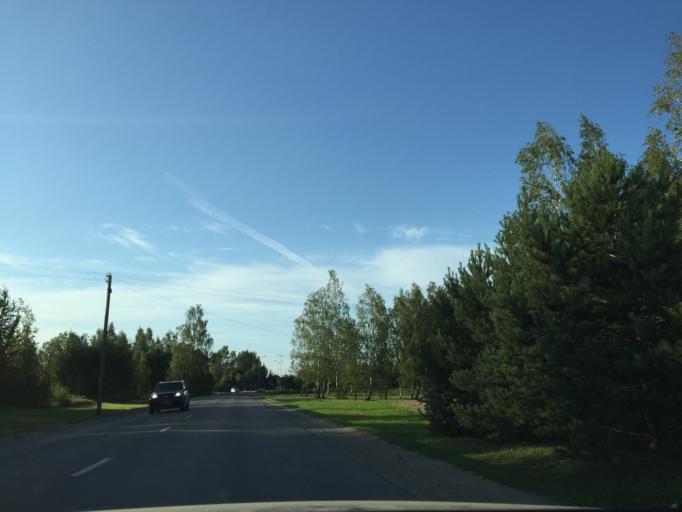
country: LT
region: Panevezys
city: Rokiskis
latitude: 55.9502
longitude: 25.5760
